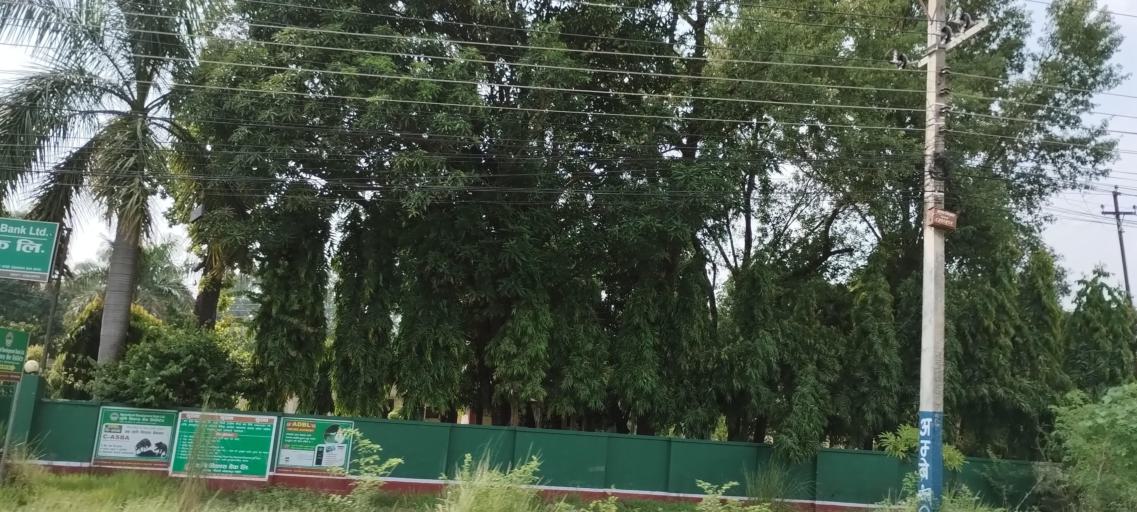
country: NP
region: Mid Western
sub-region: Bheri Zone
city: Nepalgunj
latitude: 28.1632
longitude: 81.6728
